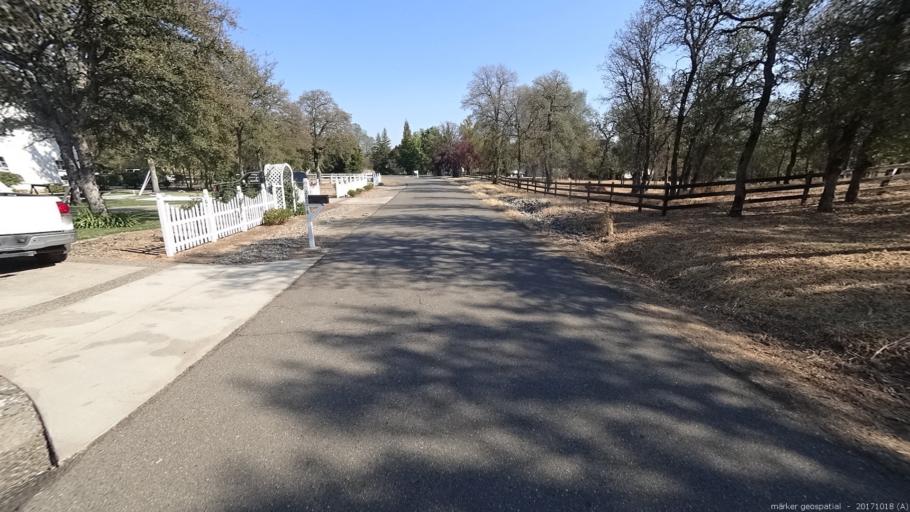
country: US
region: California
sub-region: Shasta County
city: Palo Cedro
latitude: 40.5655
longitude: -122.2341
